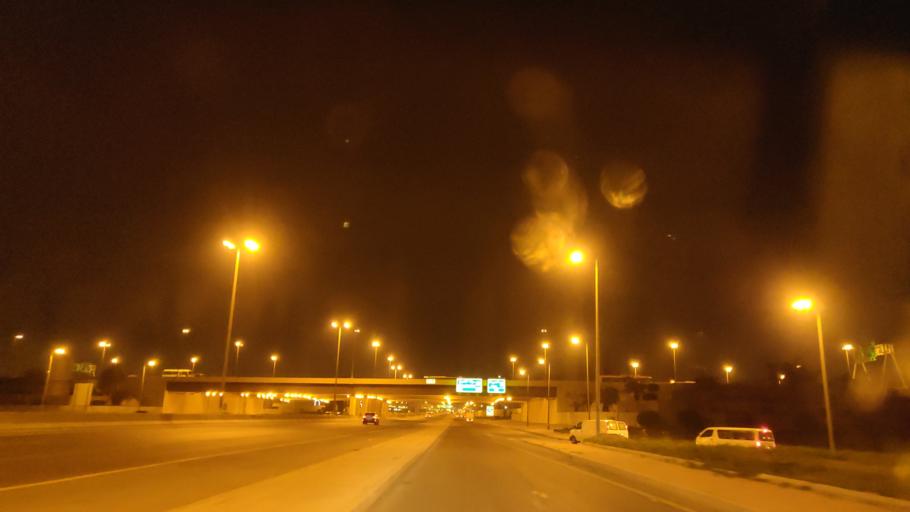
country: KW
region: Al Farwaniyah
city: Al Farwaniyah
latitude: 29.2645
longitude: 47.9527
